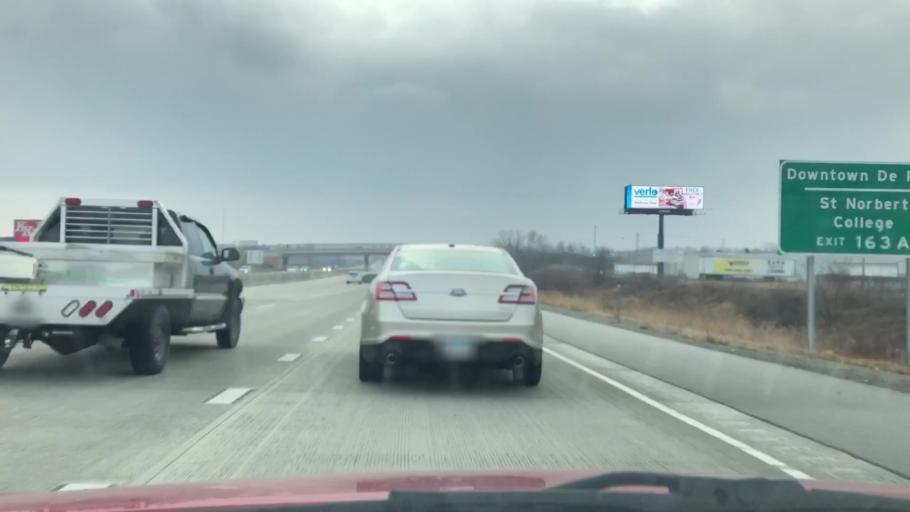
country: US
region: Wisconsin
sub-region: Brown County
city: Ashwaubenon
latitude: 44.4627
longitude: -88.0832
